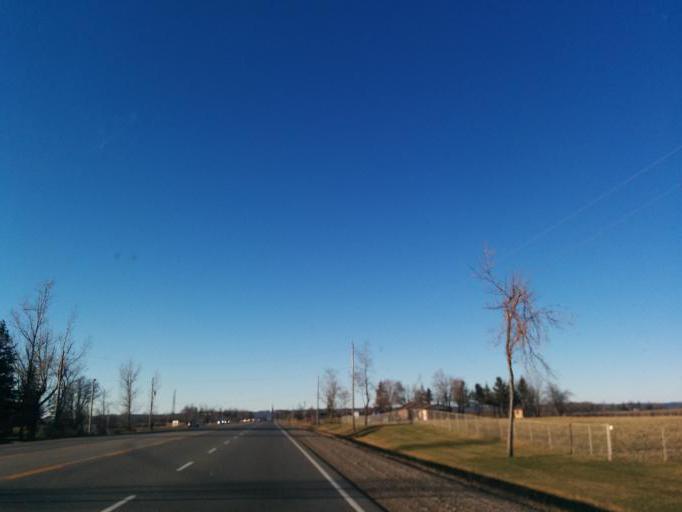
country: CA
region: Ontario
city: Brampton
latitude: 43.7882
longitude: -79.8980
